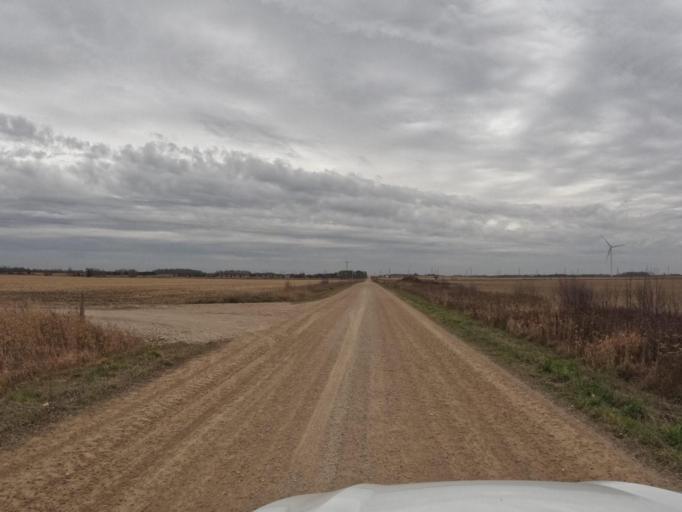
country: CA
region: Ontario
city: Shelburne
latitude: 44.0172
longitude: -80.3910
